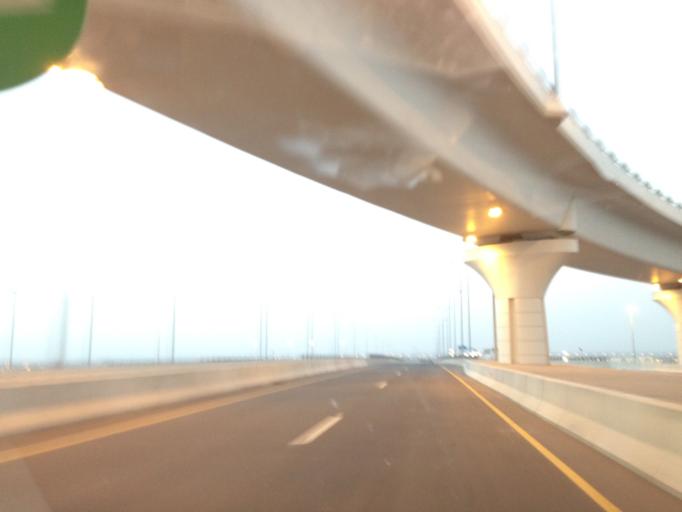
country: OM
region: Muhafazat Masqat
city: Bawshar
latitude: 23.5818
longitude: 58.3329
